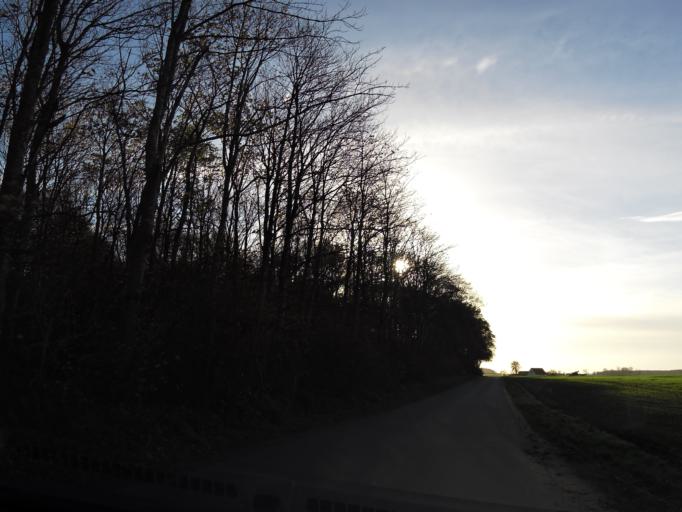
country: DK
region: Central Jutland
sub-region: Odder Kommune
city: Odder
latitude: 55.9076
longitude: 10.2253
